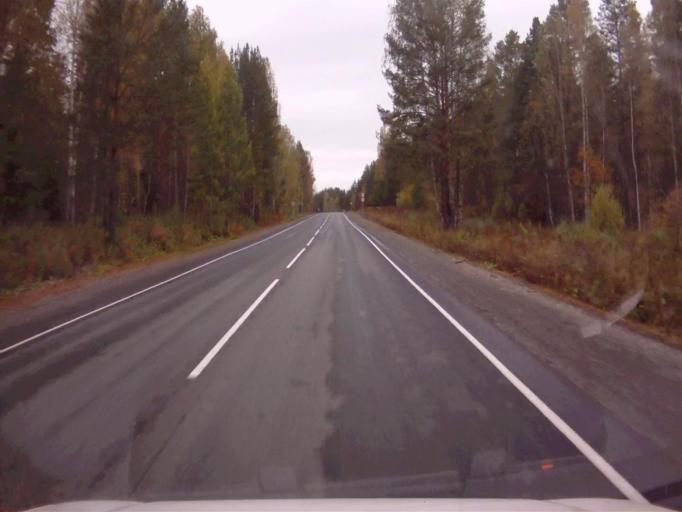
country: RU
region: Chelyabinsk
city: Nyazepetrovsk
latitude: 56.0585
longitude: 59.7330
